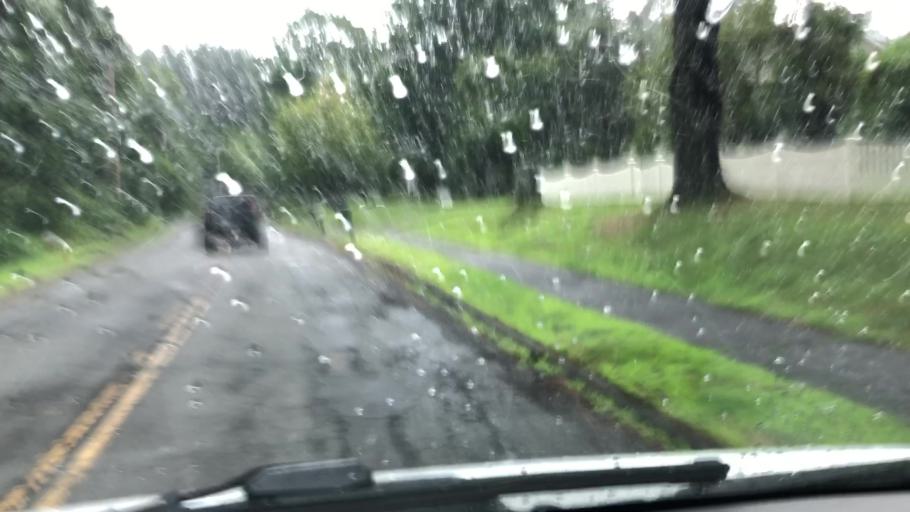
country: US
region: Massachusetts
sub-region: Hampshire County
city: Northampton
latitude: 42.3379
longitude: -72.6900
